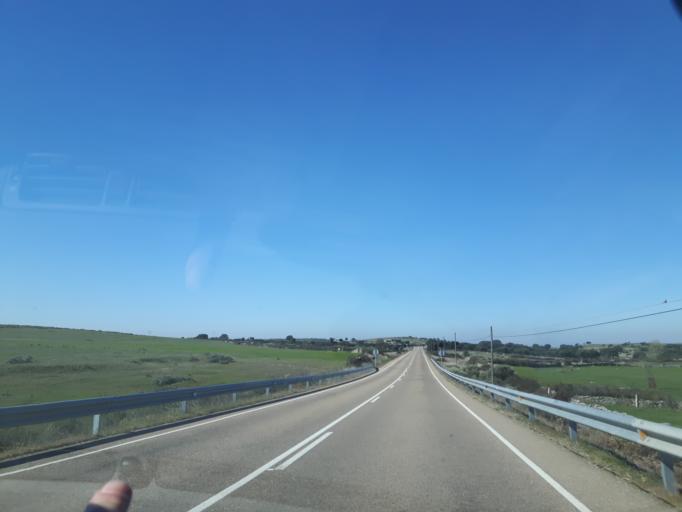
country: ES
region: Castille and Leon
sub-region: Provincia de Salamanca
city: Guadramiro
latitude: 41.0120
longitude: -6.4846
